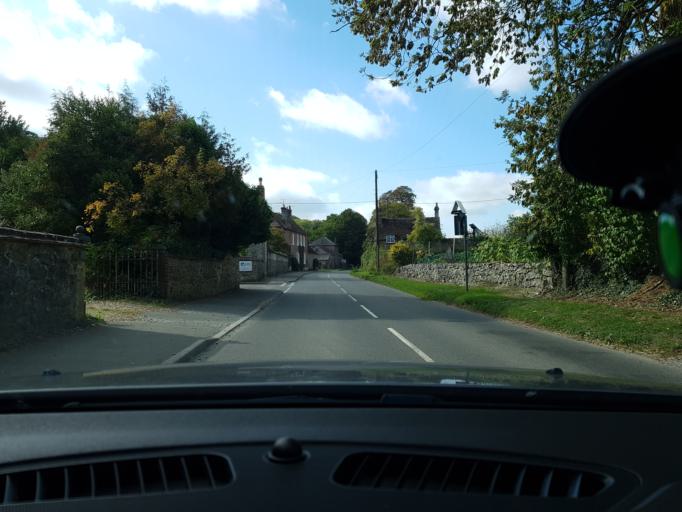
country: GB
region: England
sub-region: Wiltshire
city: Aldbourne
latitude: 51.4794
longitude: -1.6243
